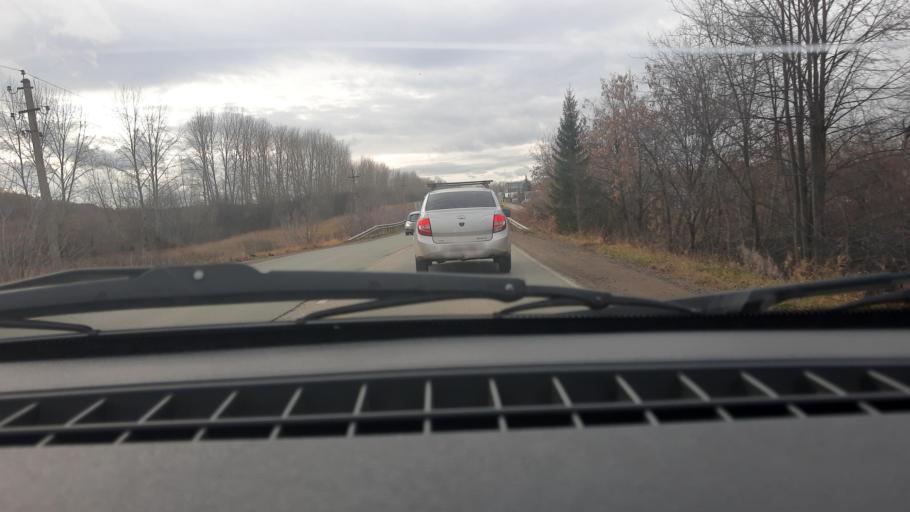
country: RU
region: Bashkortostan
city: Iglino
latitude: 54.7958
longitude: 56.3028
